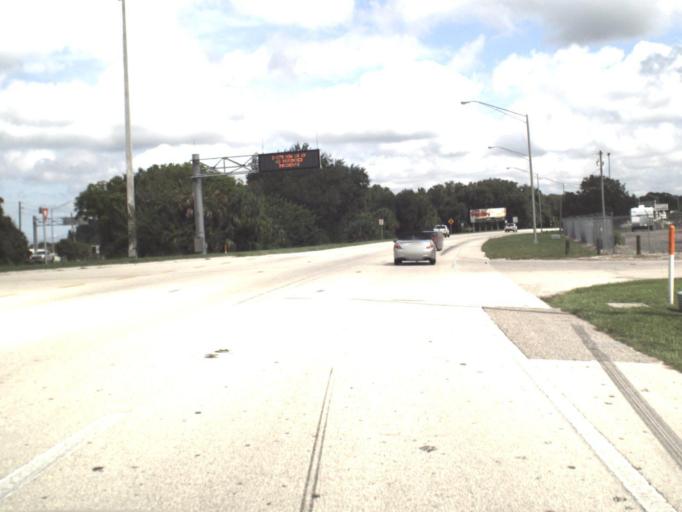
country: US
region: Florida
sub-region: Manatee County
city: Memphis
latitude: 27.5457
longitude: -82.5643
